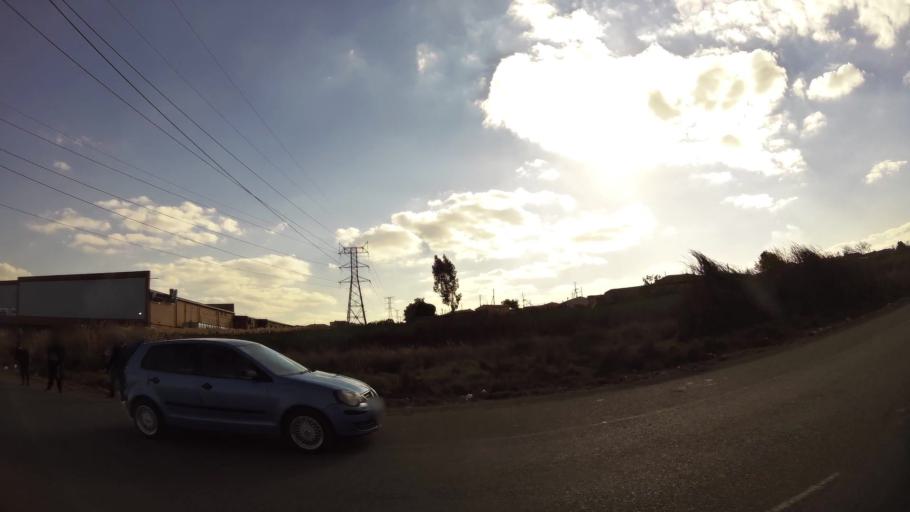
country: ZA
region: Gauteng
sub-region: Ekurhuleni Metropolitan Municipality
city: Tembisa
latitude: -25.9880
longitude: 28.1919
